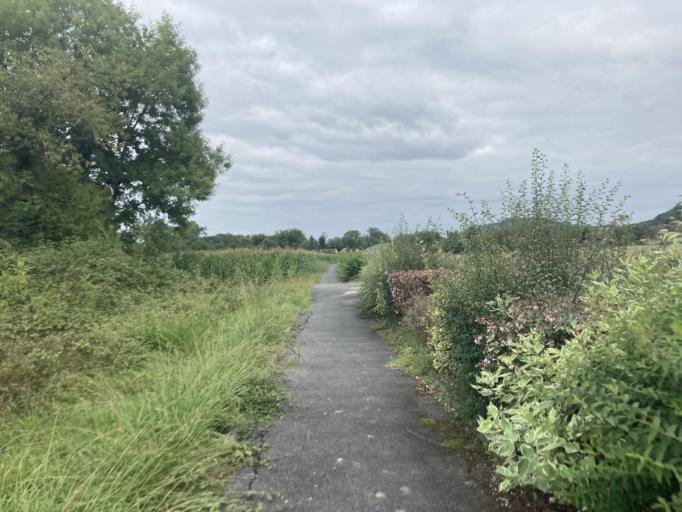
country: FR
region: Aquitaine
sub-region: Departement des Pyrenees-Atlantiques
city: Arbus
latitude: 43.3254
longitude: -0.4920
